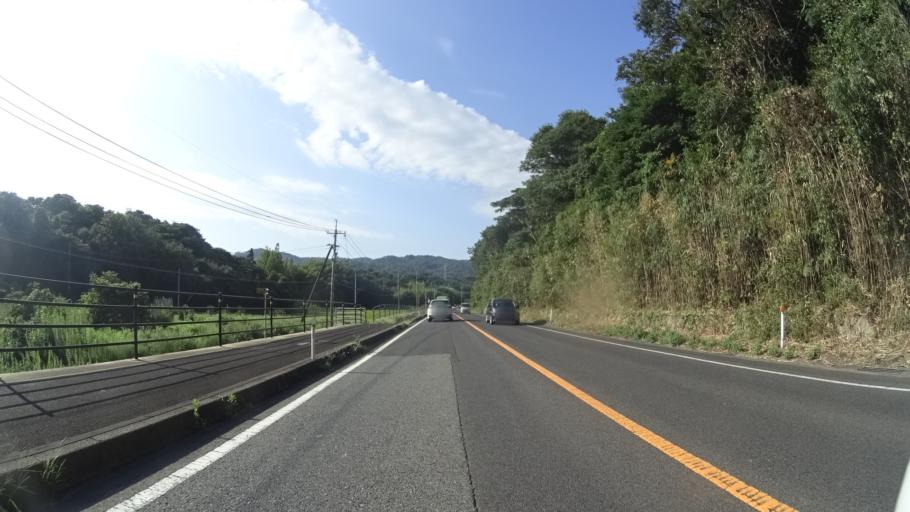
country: JP
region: Shimane
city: Izumo
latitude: 35.2983
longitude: 132.6487
